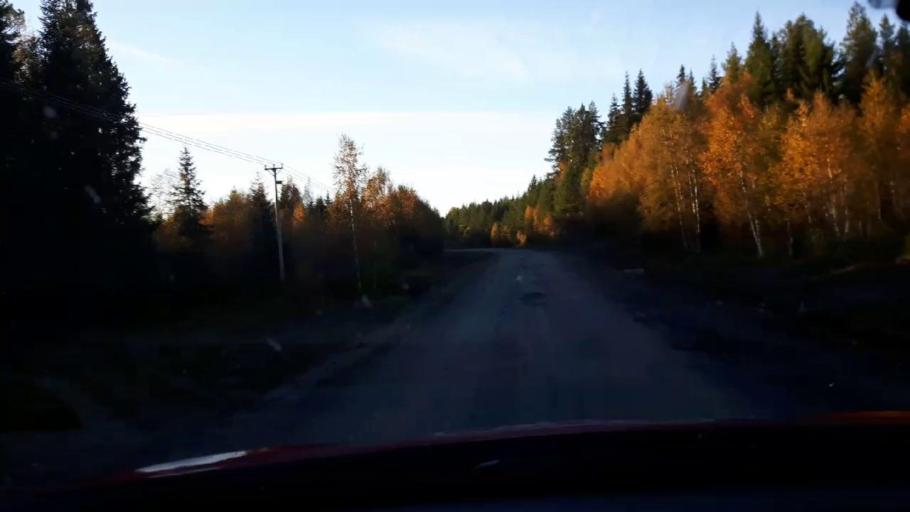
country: SE
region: Jaemtland
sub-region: Krokoms Kommun
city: Krokom
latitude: 63.4559
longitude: 14.5070
